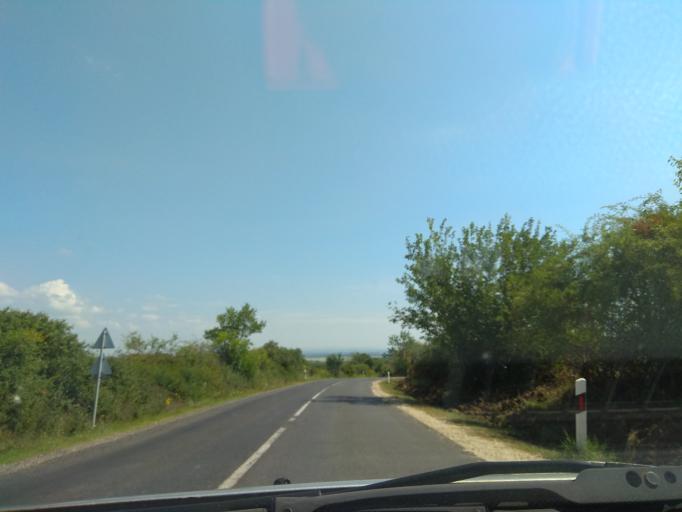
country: HU
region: Borsod-Abauj-Zemplen
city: Malyi
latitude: 48.0389
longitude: 20.7837
